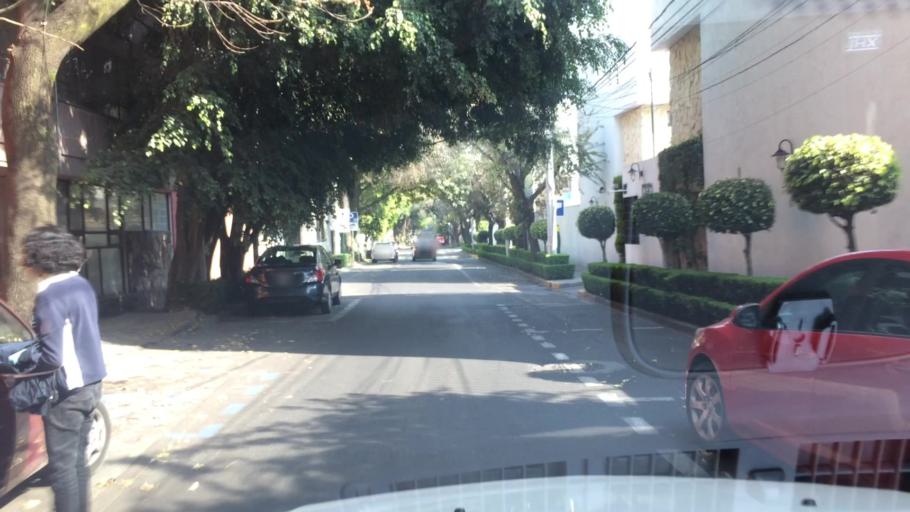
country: MX
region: Mexico City
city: Coyoacan
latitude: 19.3620
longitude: -99.1784
